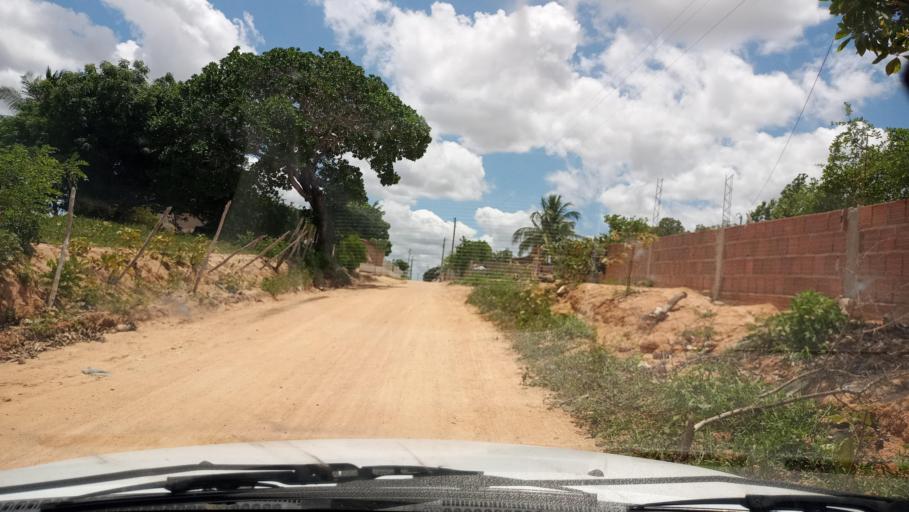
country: BR
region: Rio Grande do Norte
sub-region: Sao Jose Do Campestre
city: Sao Jose do Campestre
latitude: -6.4285
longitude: -35.6301
